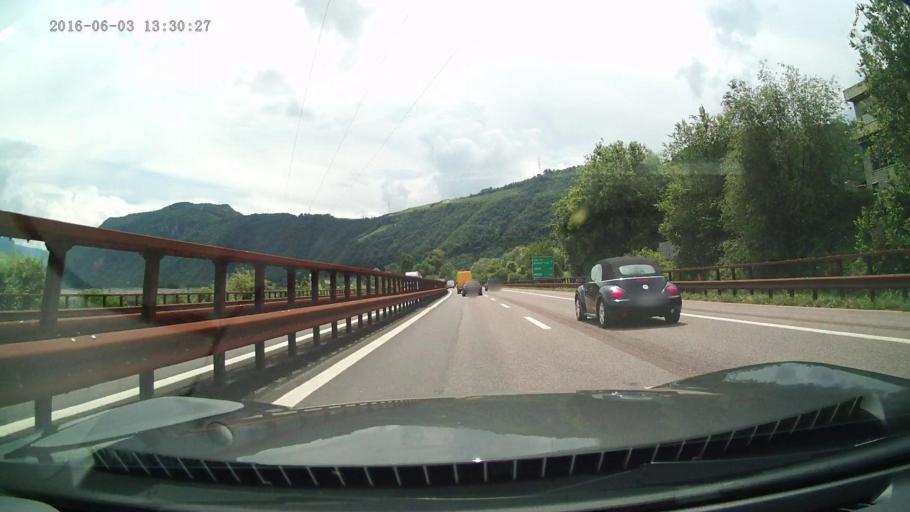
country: IT
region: Trentino-Alto Adige
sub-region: Bolzano
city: Cornaiano
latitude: 46.4661
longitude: 11.3073
